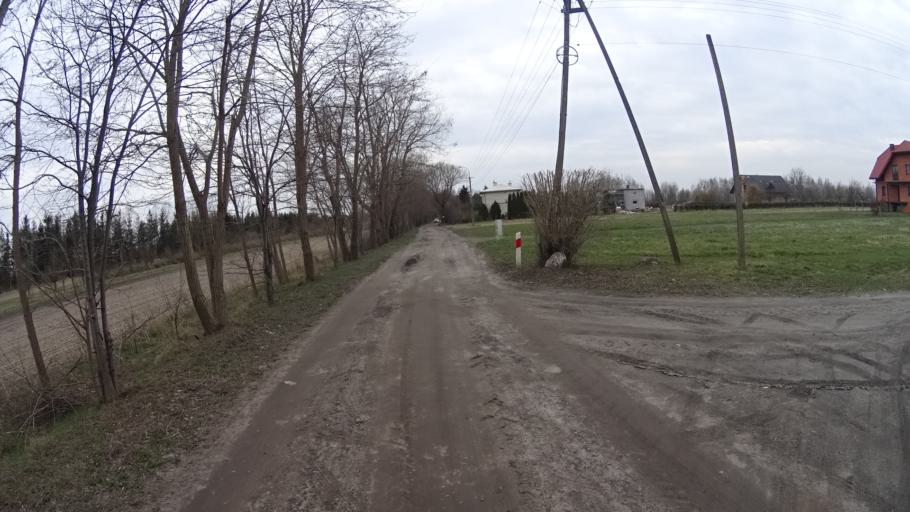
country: PL
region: Masovian Voivodeship
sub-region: Powiat warszawski zachodni
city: Jozefow
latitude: 52.2463
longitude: 20.6788
